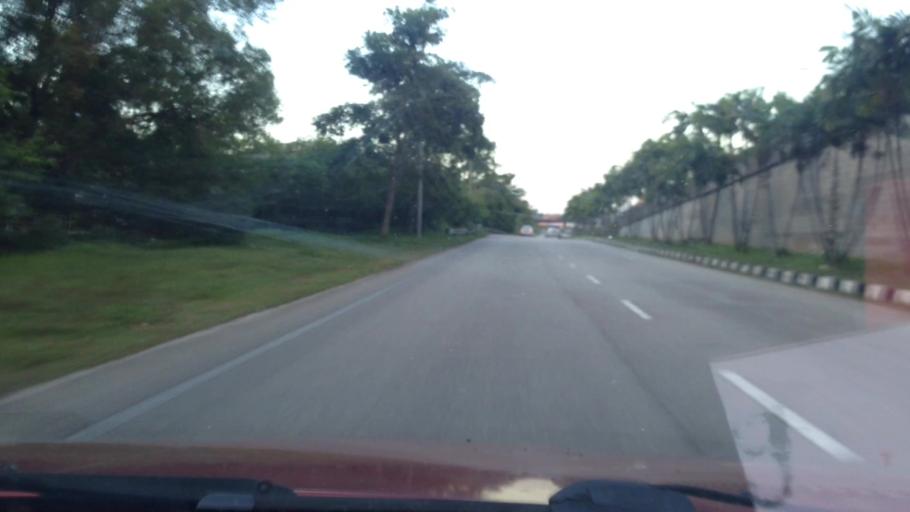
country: MY
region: Selangor
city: Shah Alam
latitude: 3.0991
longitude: 101.5482
